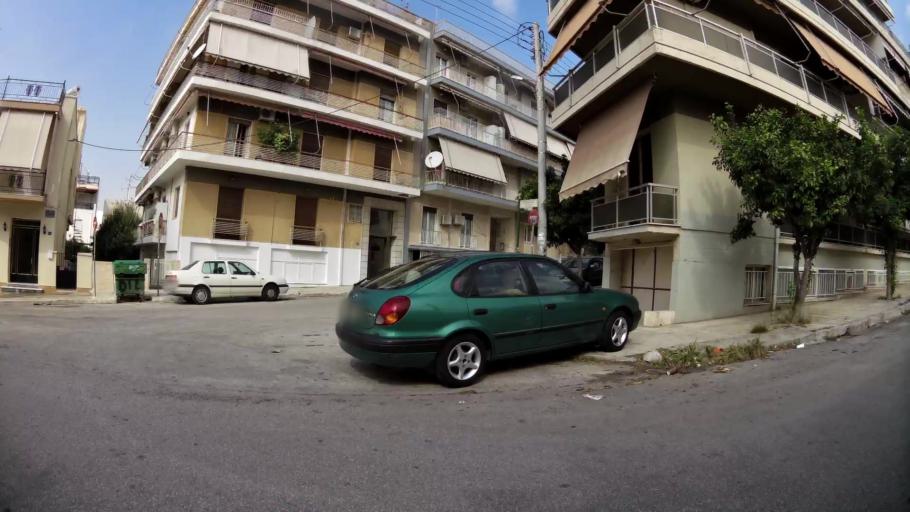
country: GR
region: Attica
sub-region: Nomarchia Athinas
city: Ilioupoli
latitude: 37.9398
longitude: 23.7580
